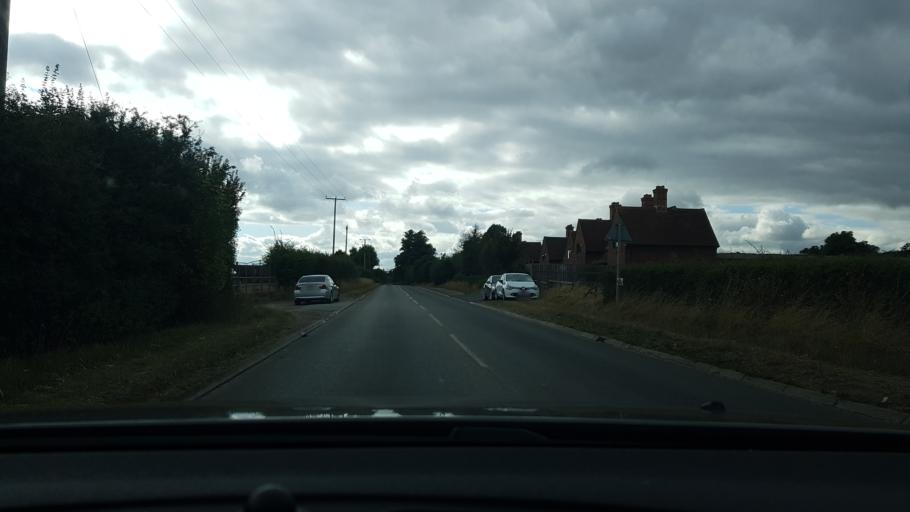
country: GB
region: England
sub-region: West Berkshire
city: Hermitage
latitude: 51.4578
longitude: -1.2948
